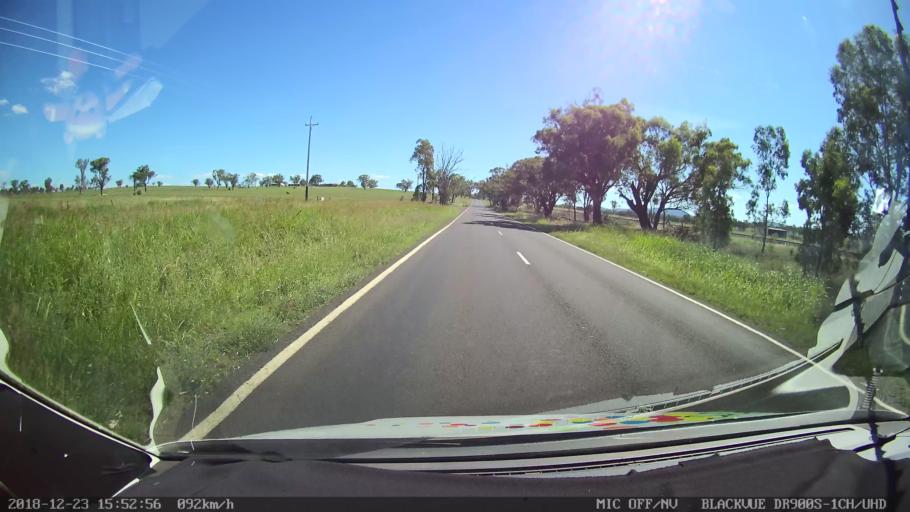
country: AU
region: New South Wales
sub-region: Tamworth Municipality
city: Phillip
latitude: -31.1272
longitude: 150.8850
